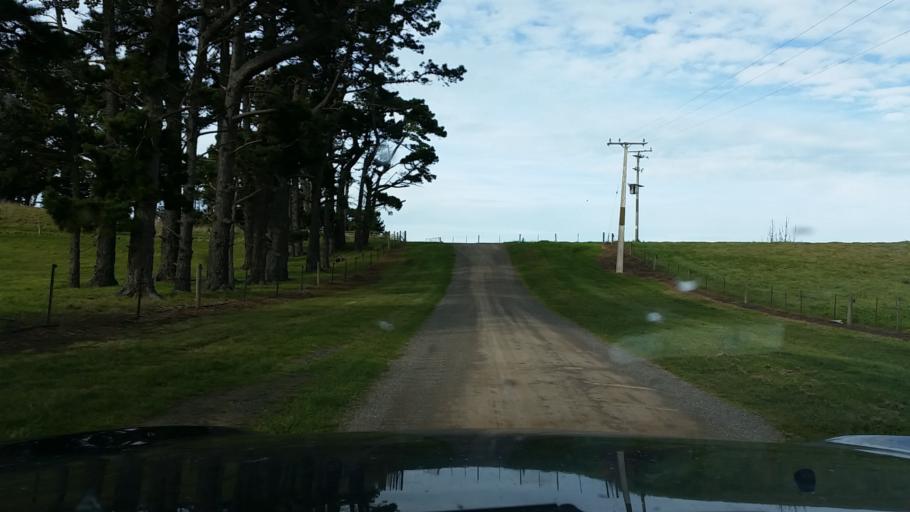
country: NZ
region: Marlborough
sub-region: Marlborough District
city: Blenheim
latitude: -41.6323
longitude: 174.1555
